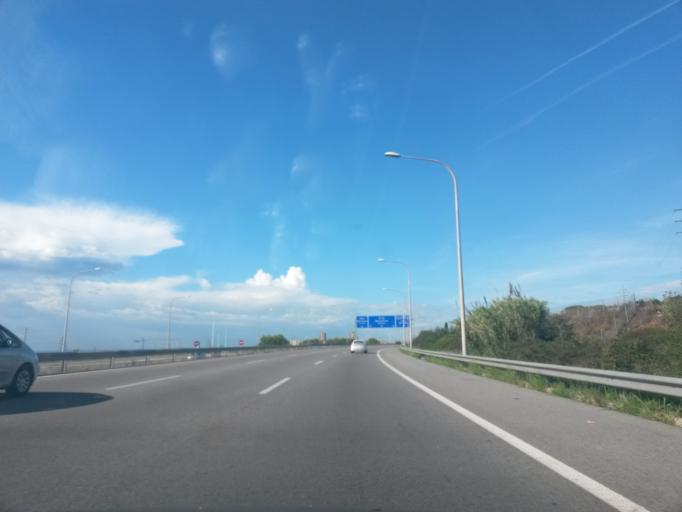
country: ES
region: Catalonia
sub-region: Provincia de Barcelona
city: Alella
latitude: 41.4816
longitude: 2.2934
